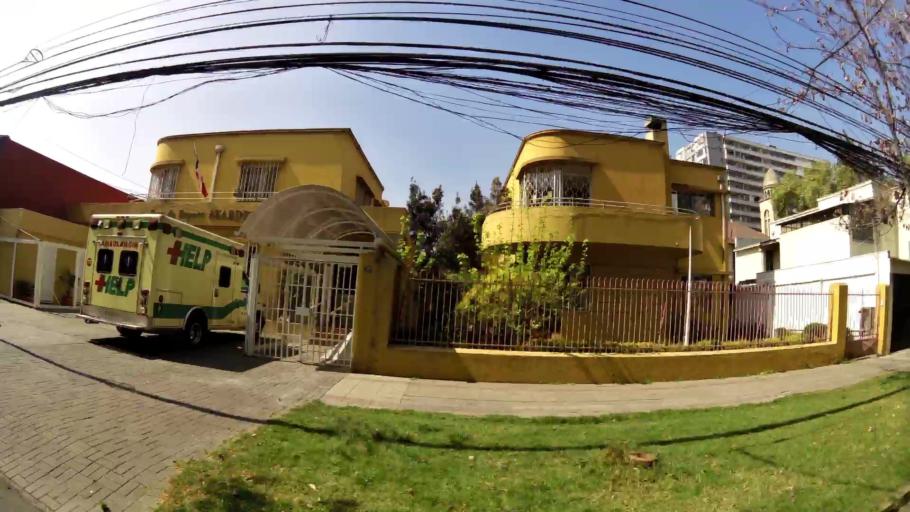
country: CL
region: Santiago Metropolitan
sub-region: Provincia de Santiago
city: Santiago
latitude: -33.4517
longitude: -70.6235
